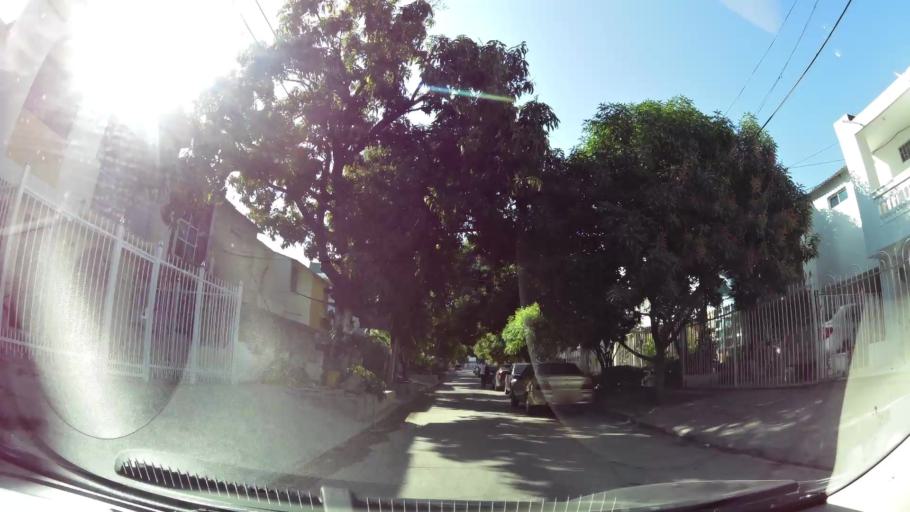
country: CO
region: Bolivar
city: Cartagena
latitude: 10.3927
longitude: -75.4952
